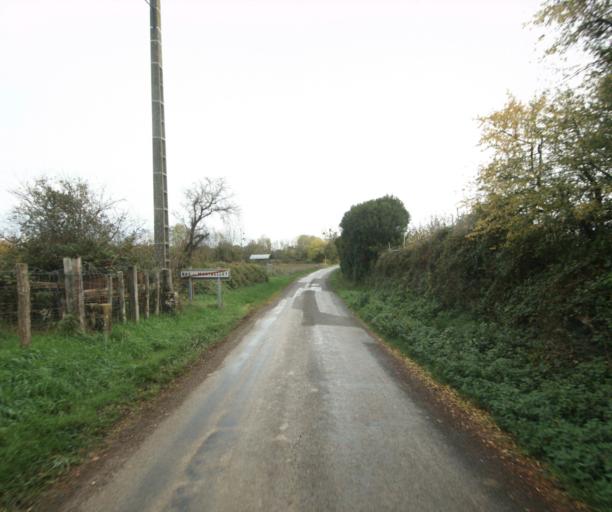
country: FR
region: Rhone-Alpes
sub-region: Departement de l'Ain
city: Pont-de-Vaux
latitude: 46.4714
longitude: 4.8883
